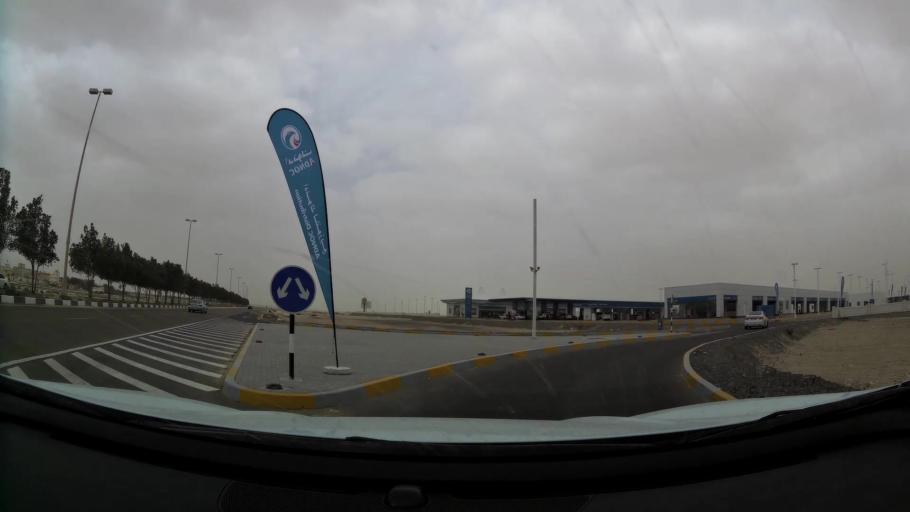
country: AE
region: Abu Dhabi
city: Abu Dhabi
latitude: 24.3981
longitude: 54.6916
